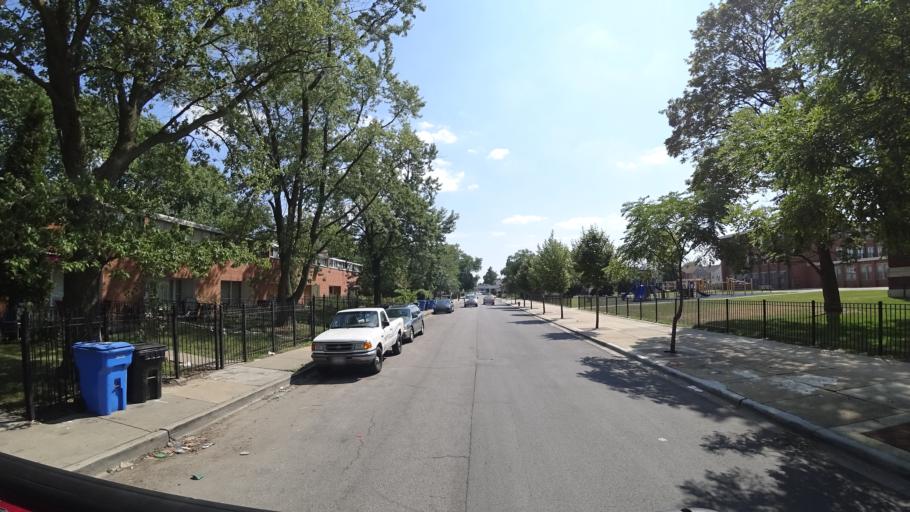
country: US
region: Illinois
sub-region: Cook County
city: Cicero
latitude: 41.8557
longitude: -87.7297
